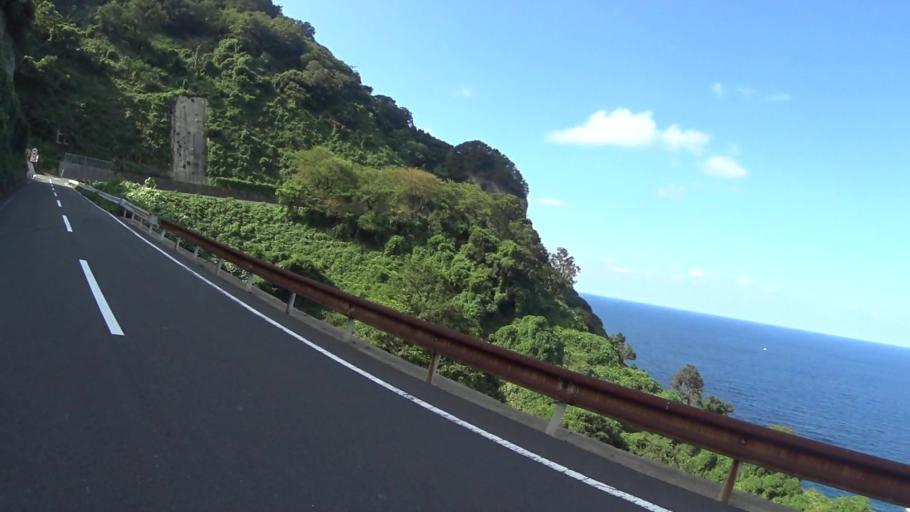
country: JP
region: Kyoto
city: Miyazu
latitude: 35.7643
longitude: 135.2354
